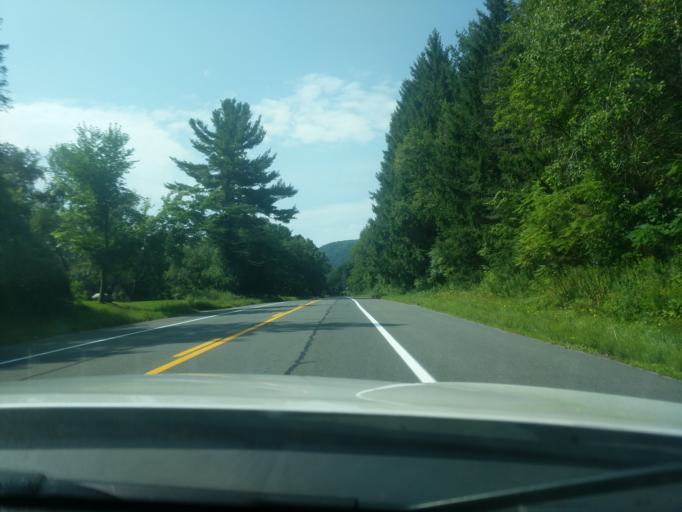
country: US
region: Massachusetts
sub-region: Berkshire County
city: Stockbridge
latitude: 42.2730
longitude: -73.3220
